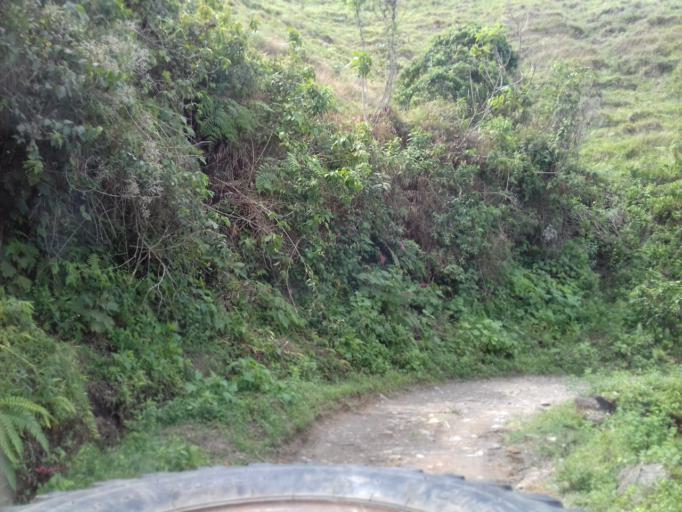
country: CO
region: Tolima
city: Libano
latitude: 4.9290
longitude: -75.0821
